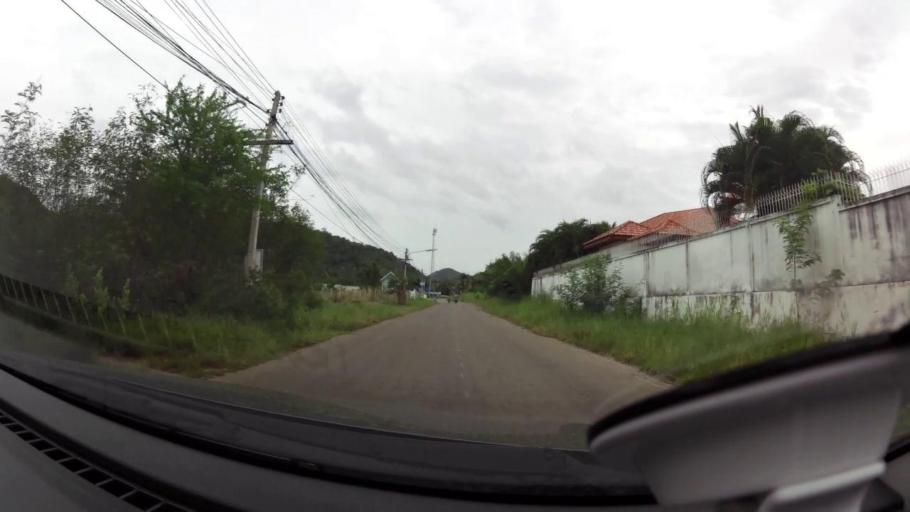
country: TH
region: Prachuap Khiri Khan
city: Pran Buri
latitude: 12.4493
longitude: 99.9713
